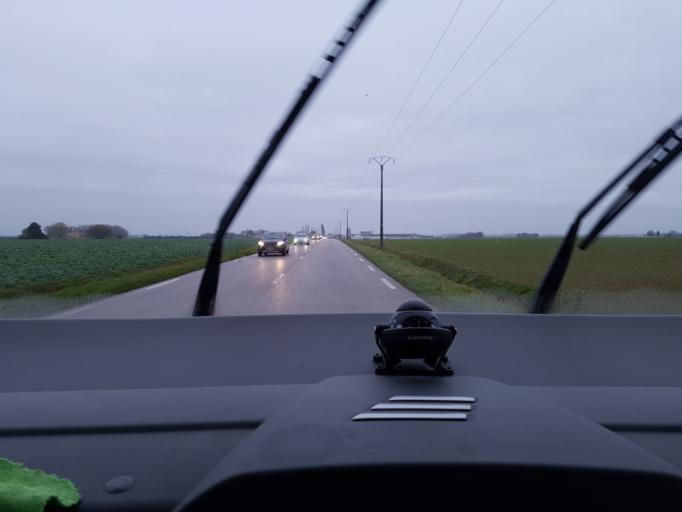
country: FR
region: Haute-Normandie
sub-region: Departement de l'Eure
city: Le Neubourg
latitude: 49.1486
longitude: 0.9260
